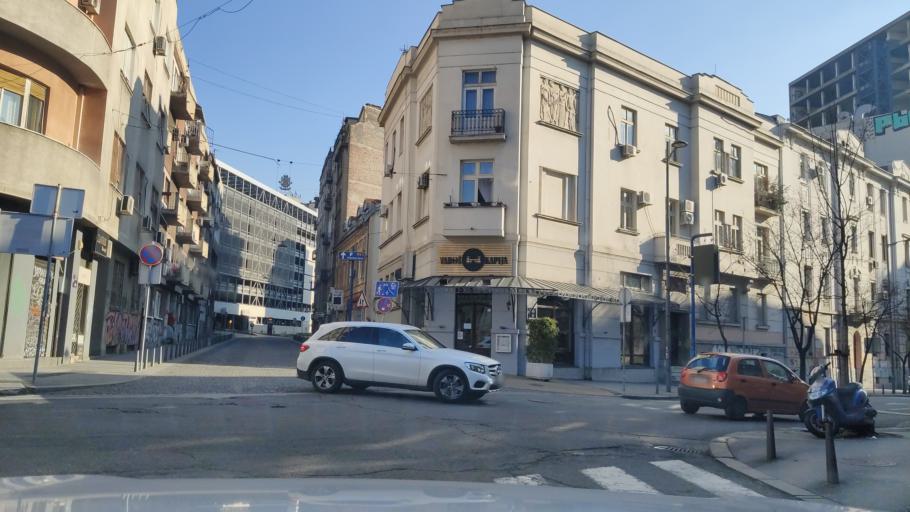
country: RS
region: Central Serbia
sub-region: Belgrade
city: Stari Grad
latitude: 44.8158
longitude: 20.4558
